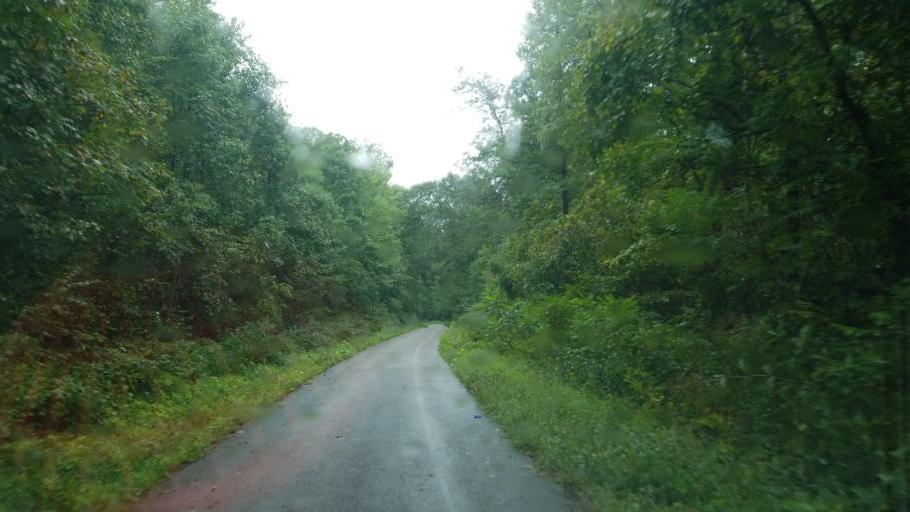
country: US
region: Ohio
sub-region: Scioto County
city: West Portsmouth
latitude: 38.7749
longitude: -83.1524
